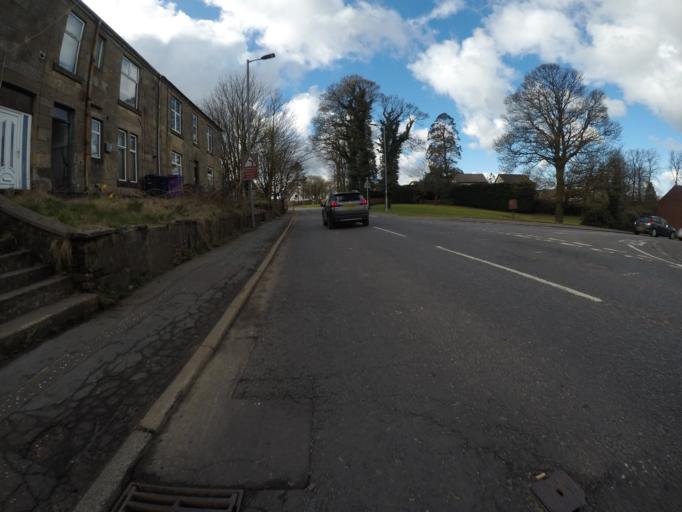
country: GB
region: Scotland
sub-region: North Ayrshire
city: Beith
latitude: 55.7470
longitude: -4.6391
